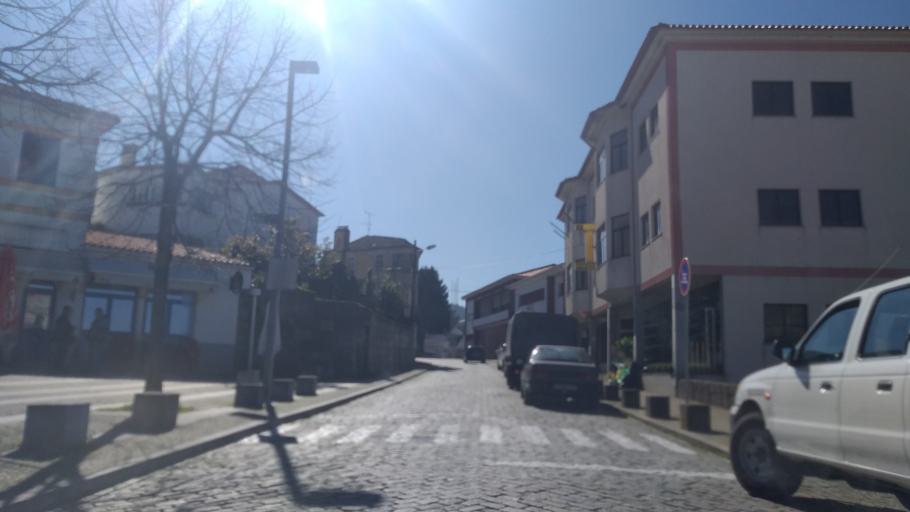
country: PT
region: Guarda
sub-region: Manteigas
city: Manteigas
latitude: 40.4927
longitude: -7.5928
